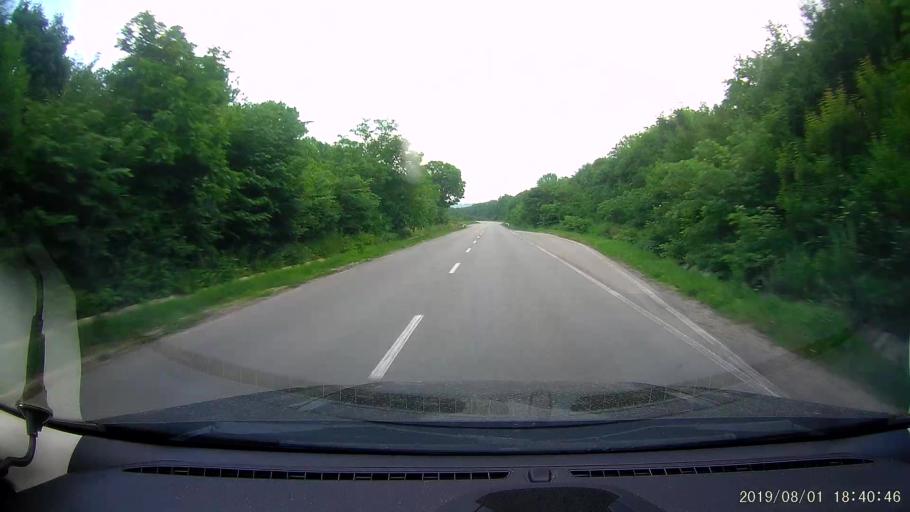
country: BG
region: Shumen
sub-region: Obshtina Khitrino
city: Gara Khitrino
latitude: 43.3595
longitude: 26.9207
